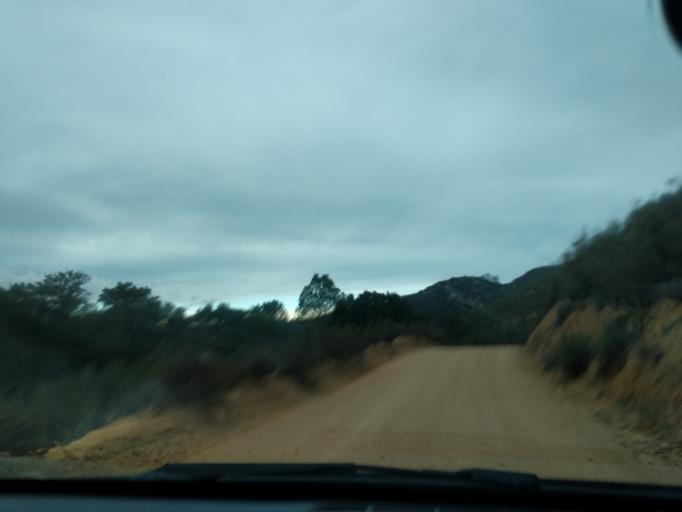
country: US
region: California
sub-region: Monterey County
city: Soledad
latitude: 36.5657
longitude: -121.2140
